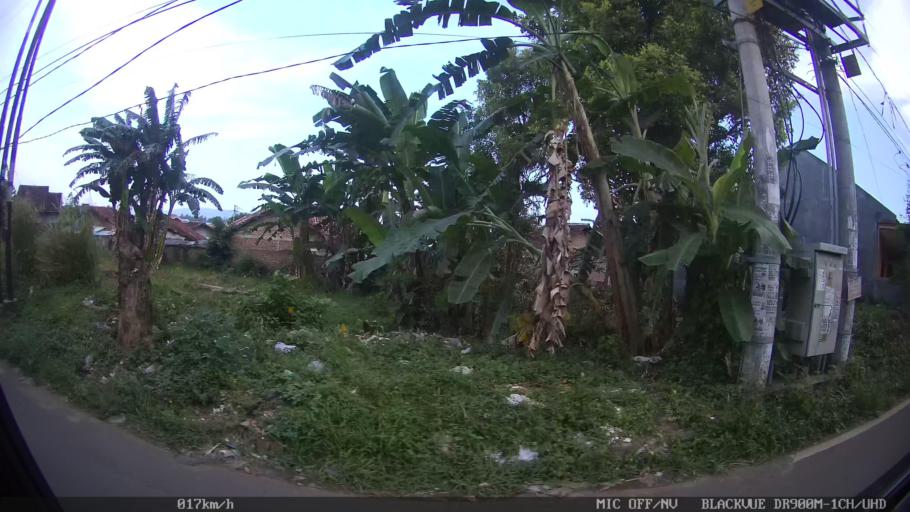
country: ID
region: Lampung
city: Kedaton
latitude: -5.3892
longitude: 105.2272
